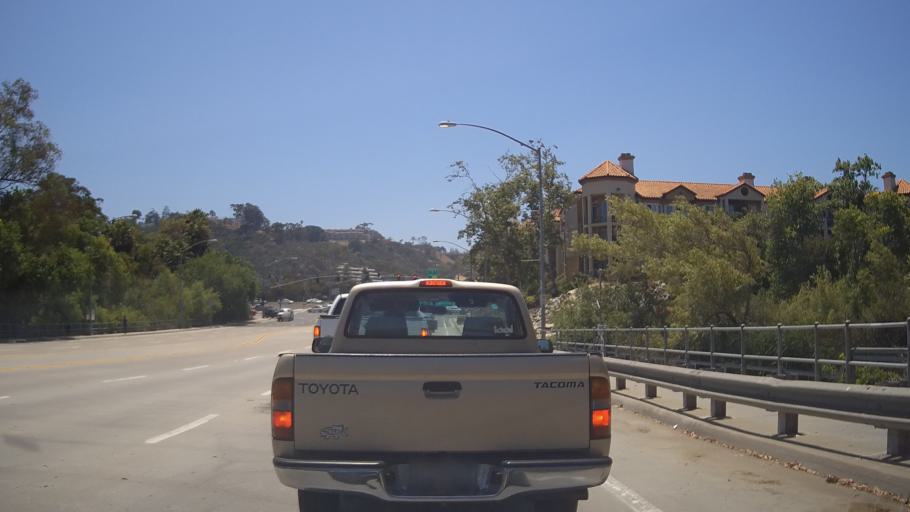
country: US
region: California
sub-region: San Diego County
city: San Diego
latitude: 32.7733
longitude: -117.1406
